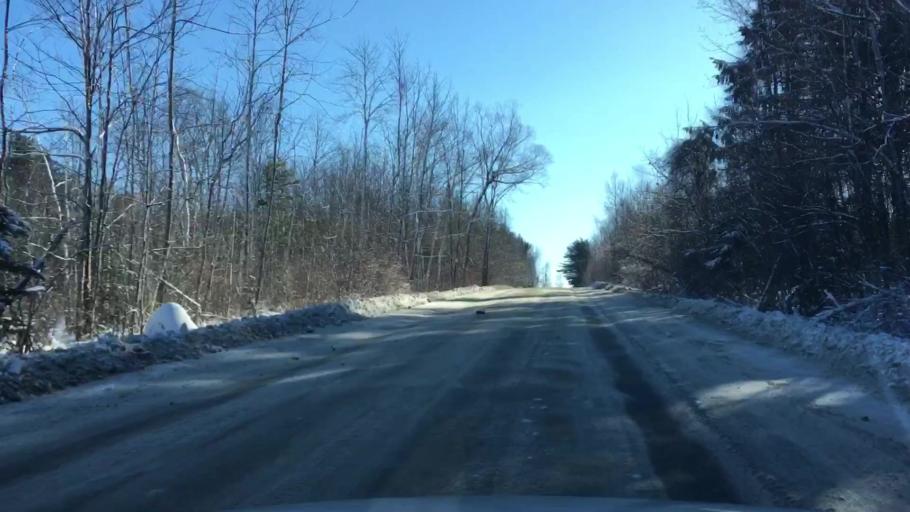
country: US
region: Maine
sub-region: Kennebec County
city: Winthrop
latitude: 44.3472
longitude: -69.9900
